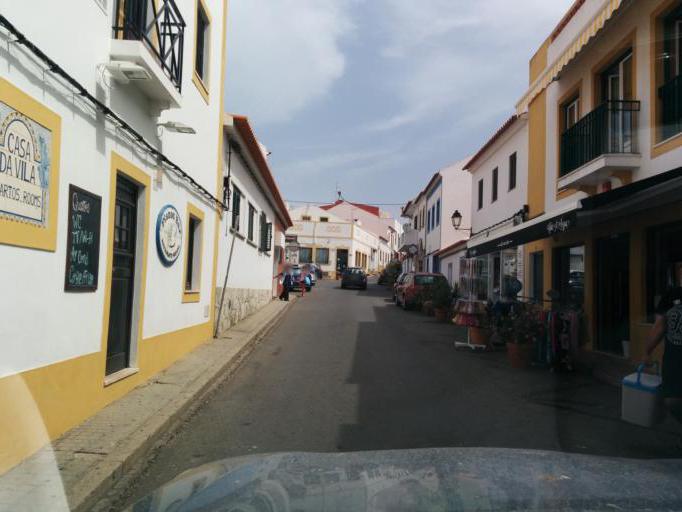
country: PT
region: Beja
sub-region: Odemira
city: Vila Nova de Milfontes
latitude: 37.7244
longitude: -8.7816
